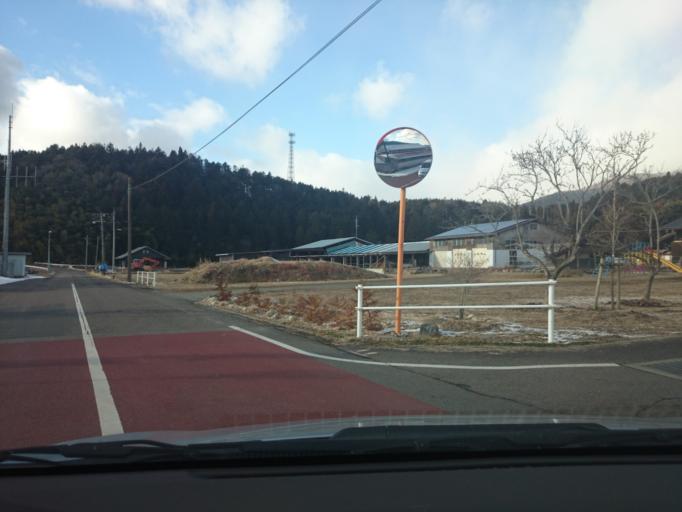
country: JP
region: Gifu
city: Nakatsugawa
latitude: 35.7520
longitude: 137.3336
